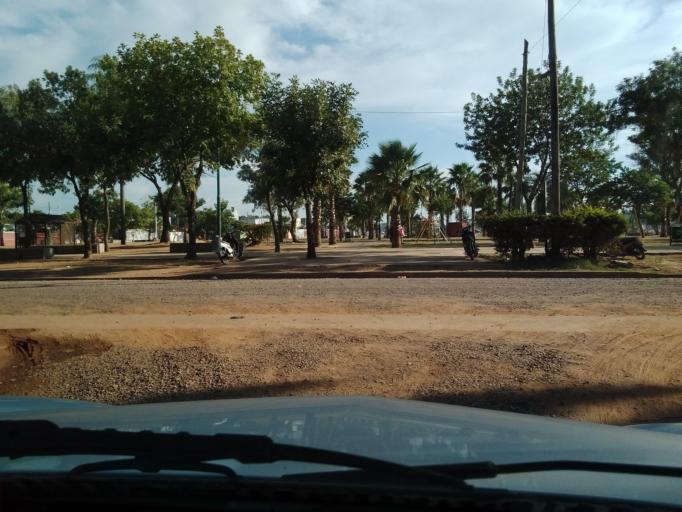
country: AR
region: Corrientes
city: Corrientes
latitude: -27.4863
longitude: -58.7833
